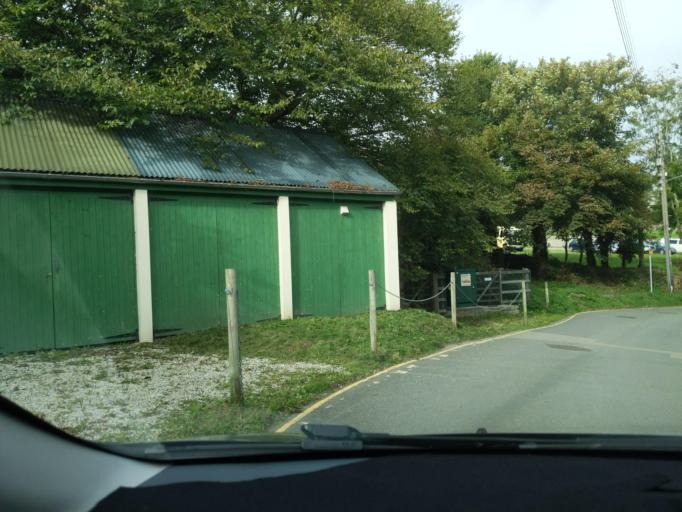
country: GB
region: England
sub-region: Cornwall
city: Mevagissey
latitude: 50.2397
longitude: -4.7920
